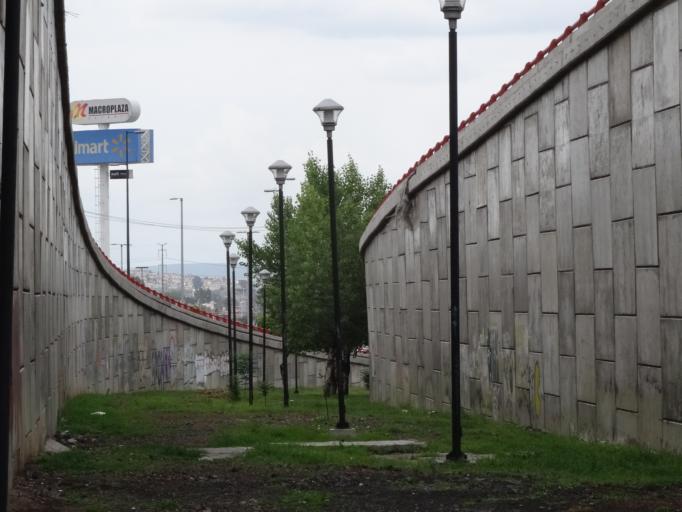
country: MX
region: Michoacan
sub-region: Tarimbaro
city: Fraccionamiento Metropolis II
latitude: 19.7256
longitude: -101.2239
